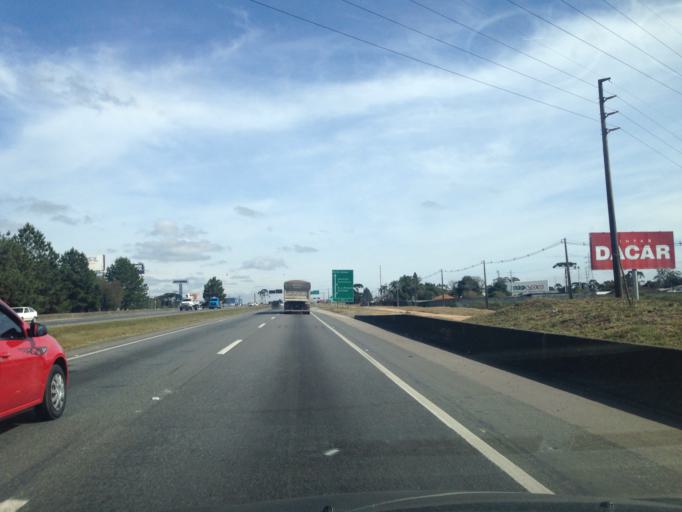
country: BR
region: Parana
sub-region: Sao Jose Dos Pinhais
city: Sao Jose dos Pinhais
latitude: -25.5667
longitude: -49.1697
